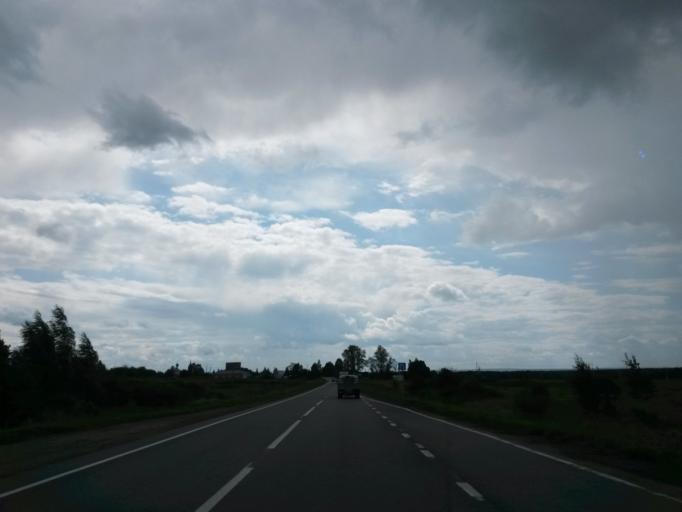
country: RU
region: Jaroslavl
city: Gavrilov-Yam
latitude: 57.3574
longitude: 39.9082
